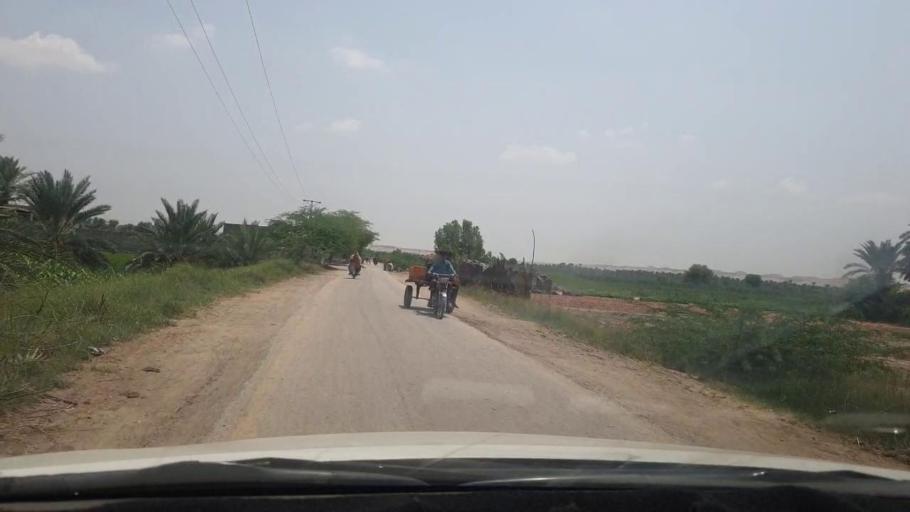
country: PK
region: Sindh
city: Khairpur
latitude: 27.5353
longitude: 68.8865
